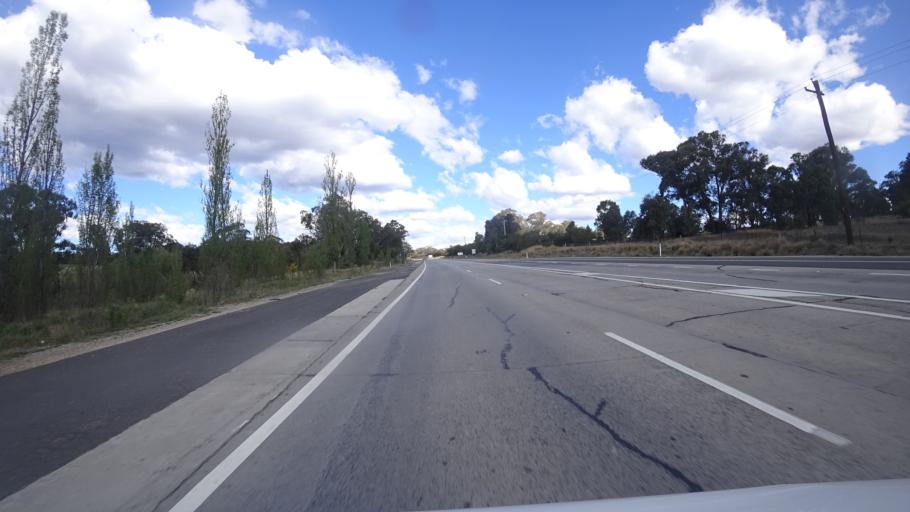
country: AU
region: New South Wales
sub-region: Lithgow
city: Bowenfels
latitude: -33.5492
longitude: 150.1823
